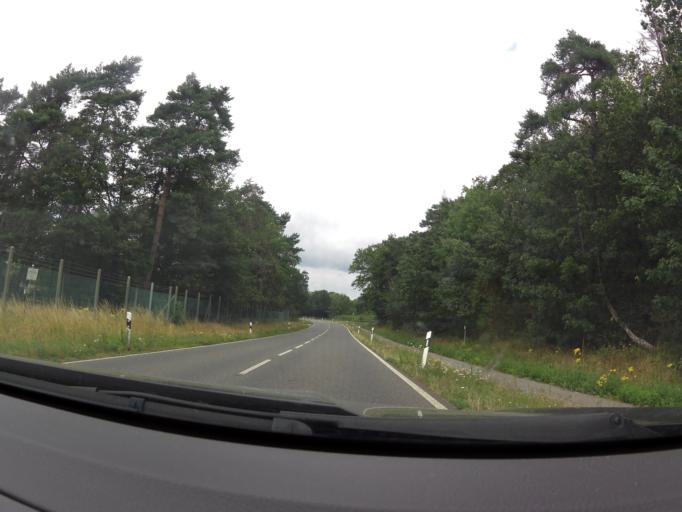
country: DE
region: North Rhine-Westphalia
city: Straelen
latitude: 51.4257
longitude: 6.2570
